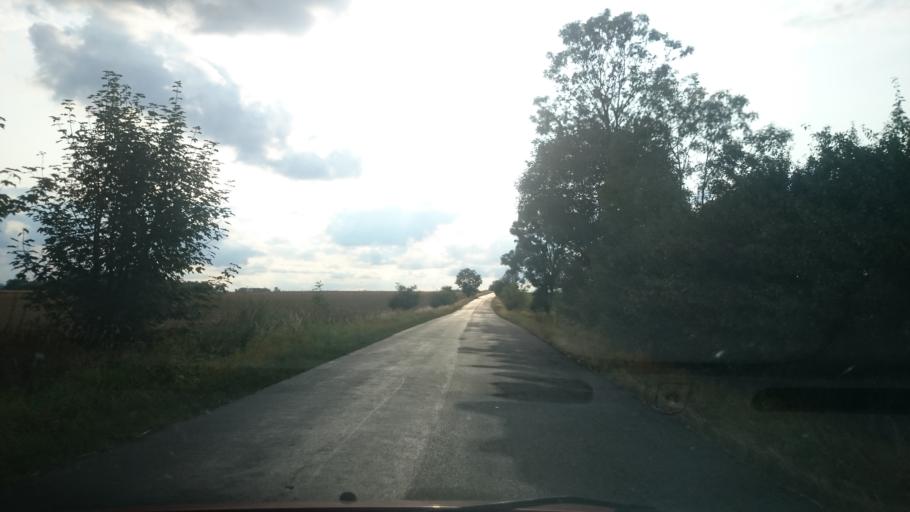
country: PL
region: Opole Voivodeship
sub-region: Powiat nyski
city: Otmuchow
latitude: 50.5067
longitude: 17.1813
